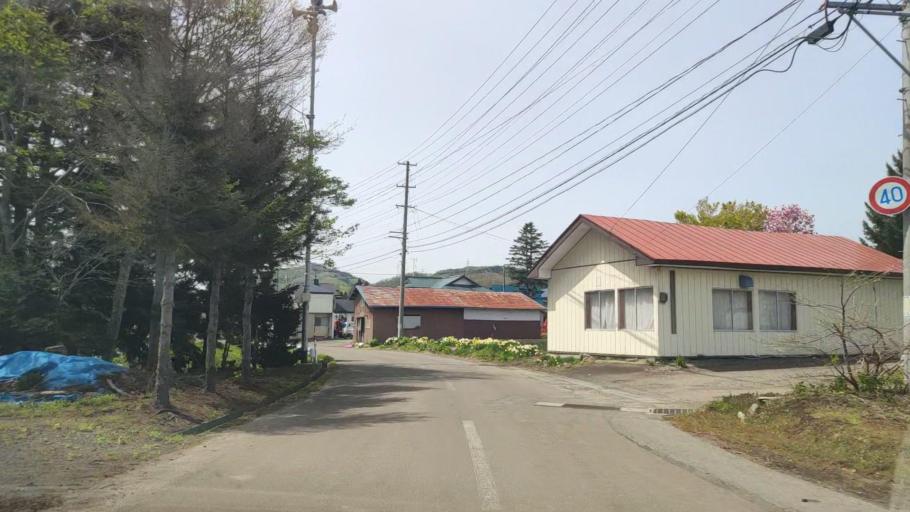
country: JP
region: Aomori
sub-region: Misawa Shi
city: Inuotose
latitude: 40.7894
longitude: 141.1093
